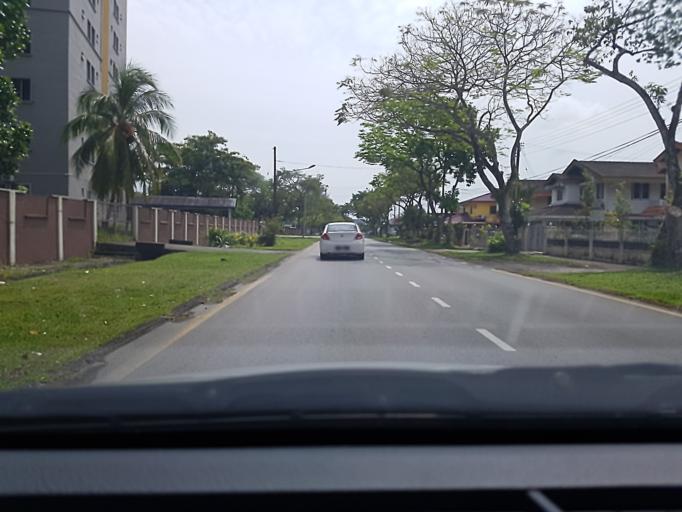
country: MY
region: Sarawak
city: Kuching
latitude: 1.5081
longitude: 110.3625
